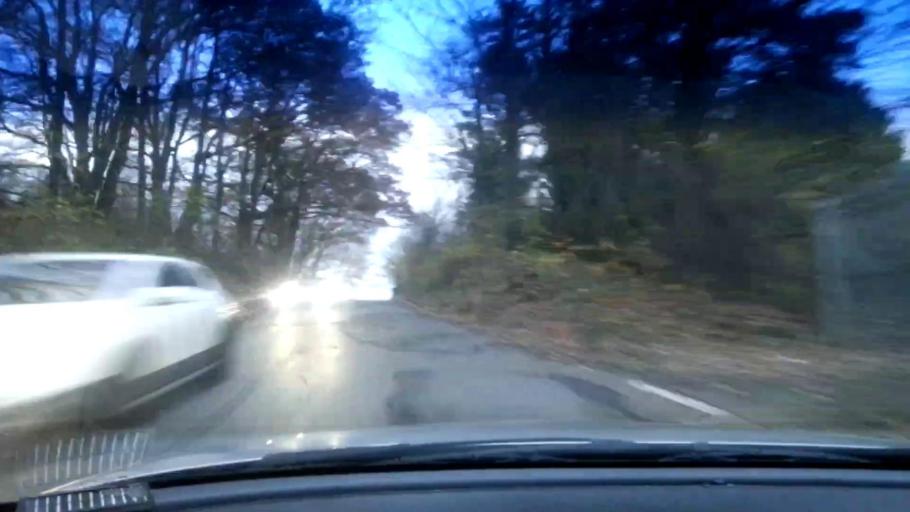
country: DE
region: Bavaria
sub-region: Upper Franconia
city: Stegaurach
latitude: 49.8840
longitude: 10.8638
